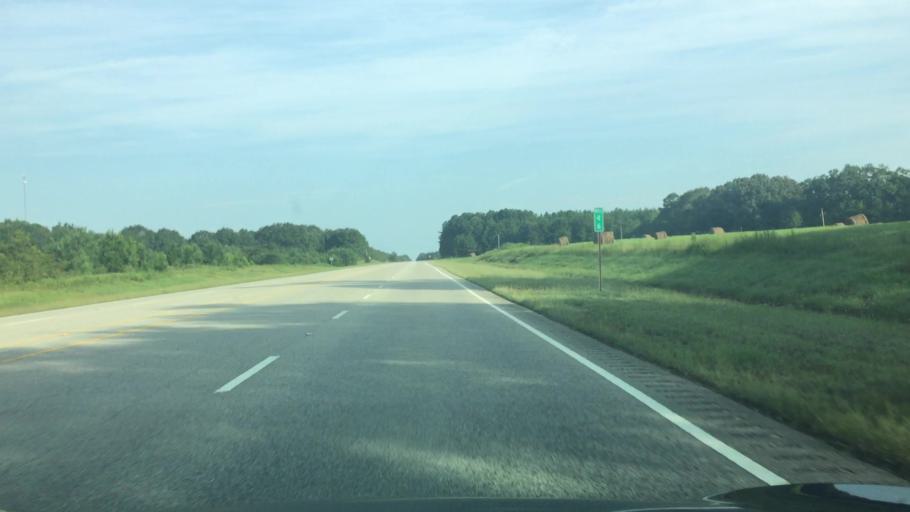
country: US
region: Alabama
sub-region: Butler County
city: Georgiana
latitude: 31.4989
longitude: -86.6936
